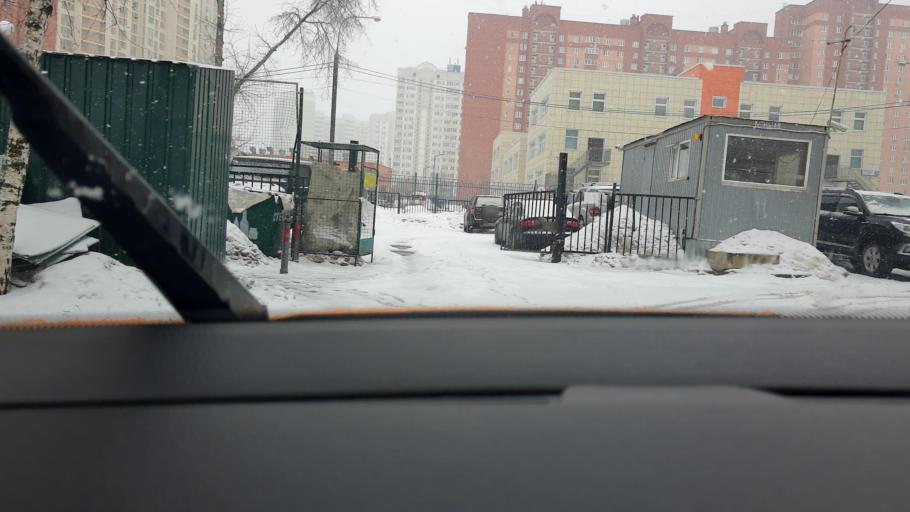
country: RU
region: Moskovskaya
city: Dolgoprudnyy
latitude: 55.9370
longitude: 37.4992
